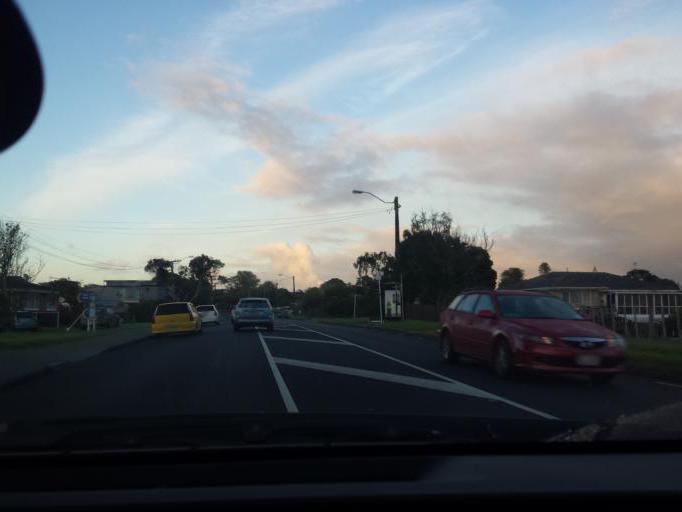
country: NZ
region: Auckland
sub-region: Auckland
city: Tamaki
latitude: -36.8715
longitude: 174.8447
